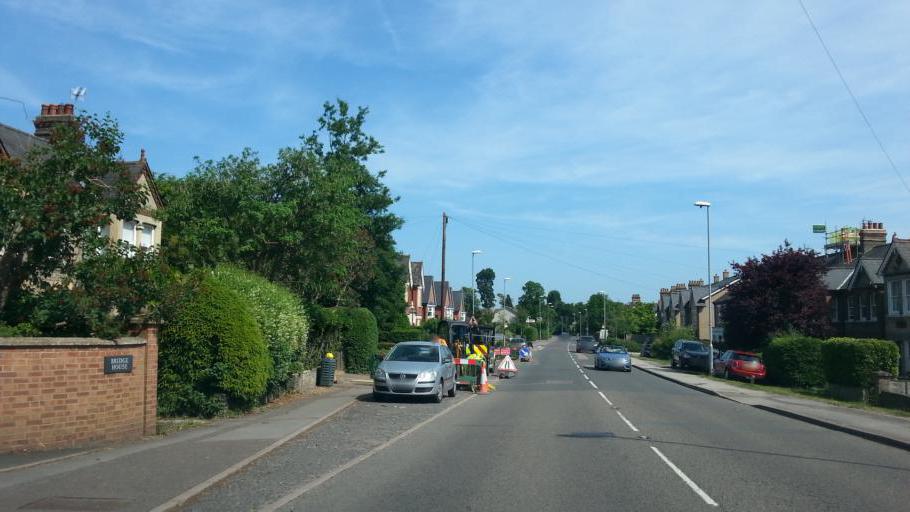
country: GB
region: England
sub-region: Cambridgeshire
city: Sawston
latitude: 52.1462
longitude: 0.1408
